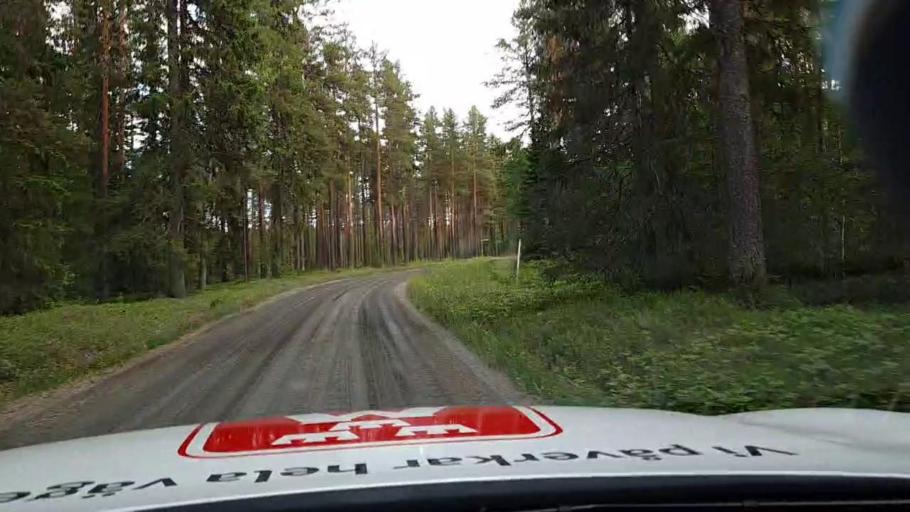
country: SE
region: Jaemtland
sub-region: OEstersunds Kommun
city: Lit
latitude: 63.5697
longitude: 14.7213
